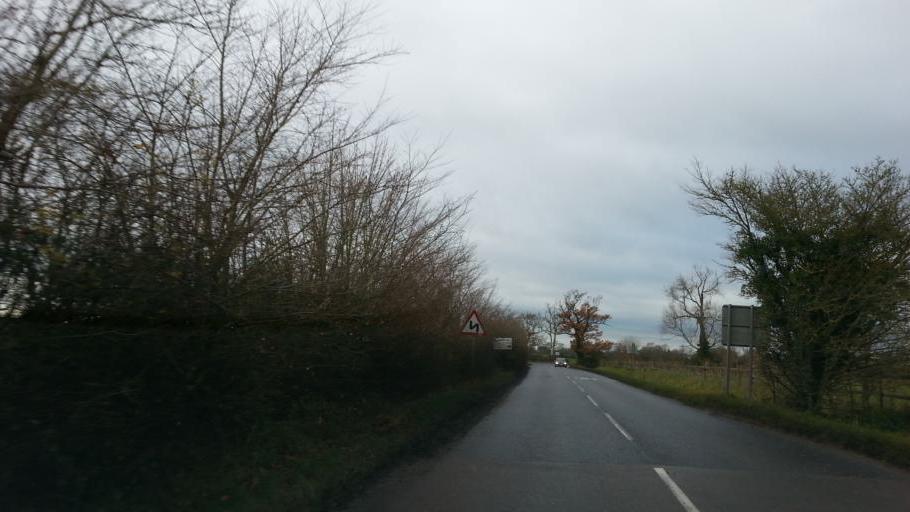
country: GB
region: England
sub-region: Suffolk
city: Framlingham
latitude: 52.3109
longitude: 1.3341
